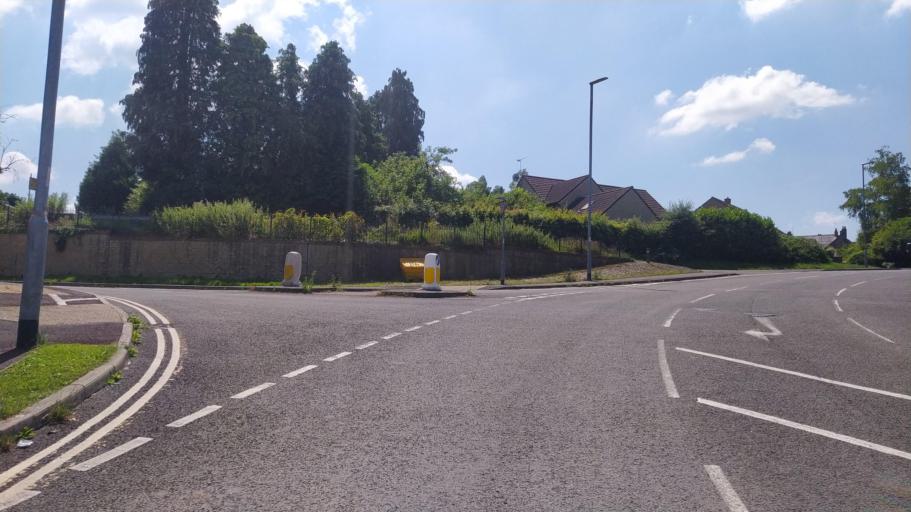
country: GB
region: England
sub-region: Somerset
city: Frome
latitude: 51.2299
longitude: -2.3157
